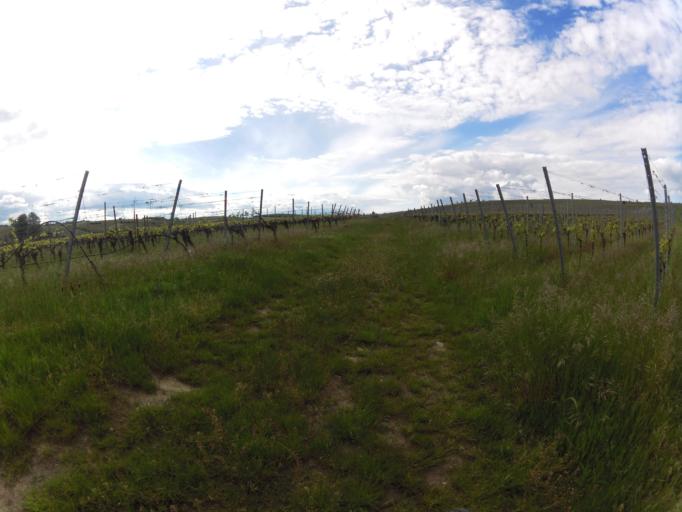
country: DE
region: Bavaria
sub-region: Regierungsbezirk Unterfranken
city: Sommerach
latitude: 49.8329
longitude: 10.1993
